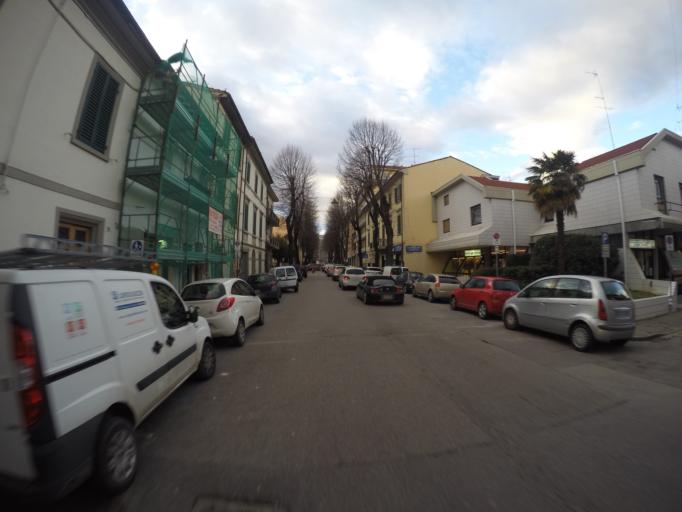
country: IT
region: Tuscany
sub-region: Provincia di Prato
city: Prato
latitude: 43.8754
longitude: 11.1062
